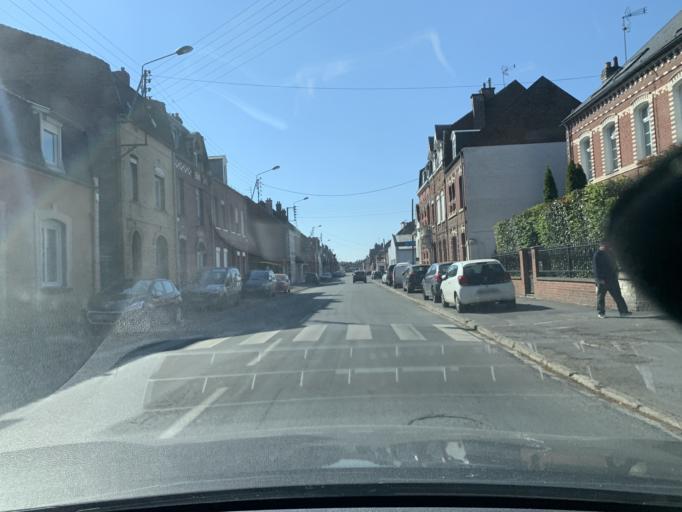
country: FR
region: Nord-Pas-de-Calais
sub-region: Departement du Nord
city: Cambrai
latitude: 50.1668
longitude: 3.2381
